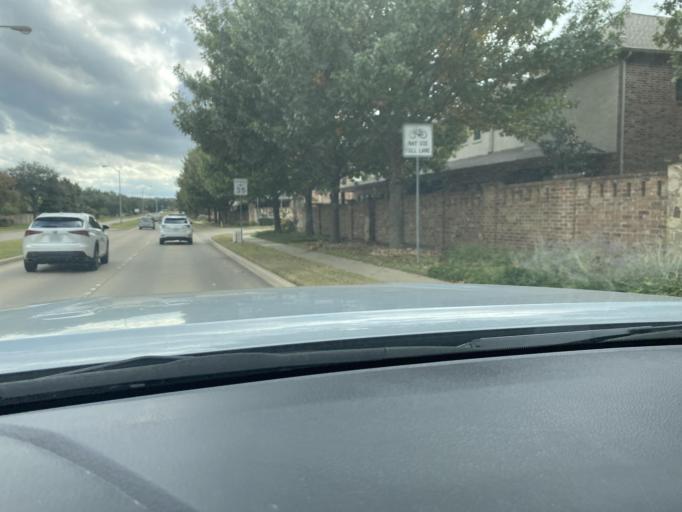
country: US
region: Texas
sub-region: Dallas County
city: Addison
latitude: 33.0416
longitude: -96.7895
